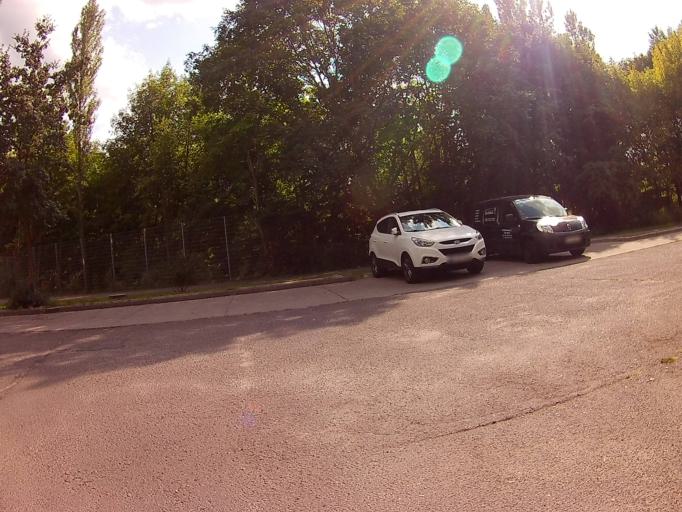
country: DE
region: Berlin
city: Friedrichsfelde
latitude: 52.4933
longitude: 13.5048
